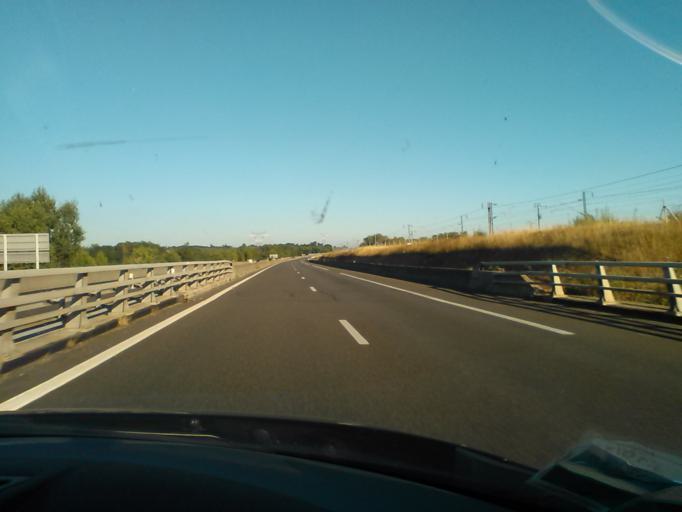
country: FR
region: Rhone-Alpes
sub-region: Departement du Rhone
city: Jonage
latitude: 45.8155
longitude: 5.0526
